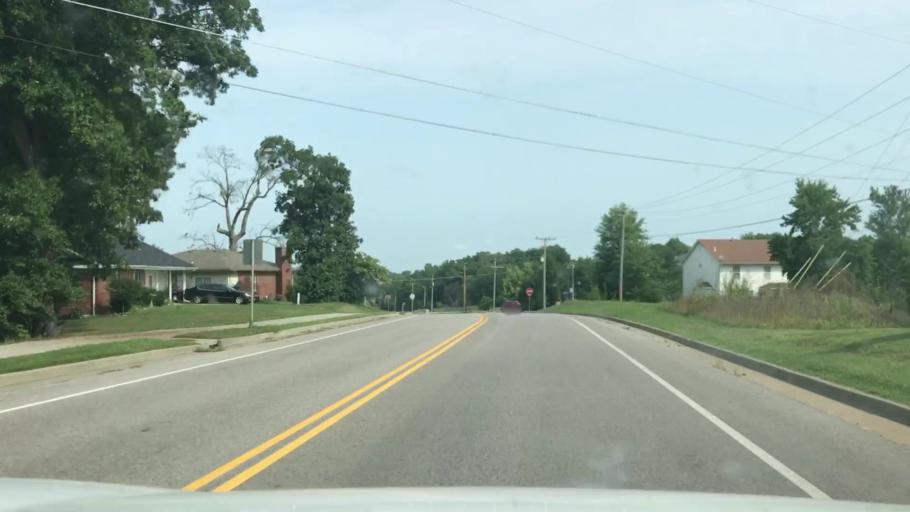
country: US
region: Missouri
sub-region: Saint Charles County
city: Cottleville
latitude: 38.7166
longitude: -90.6418
